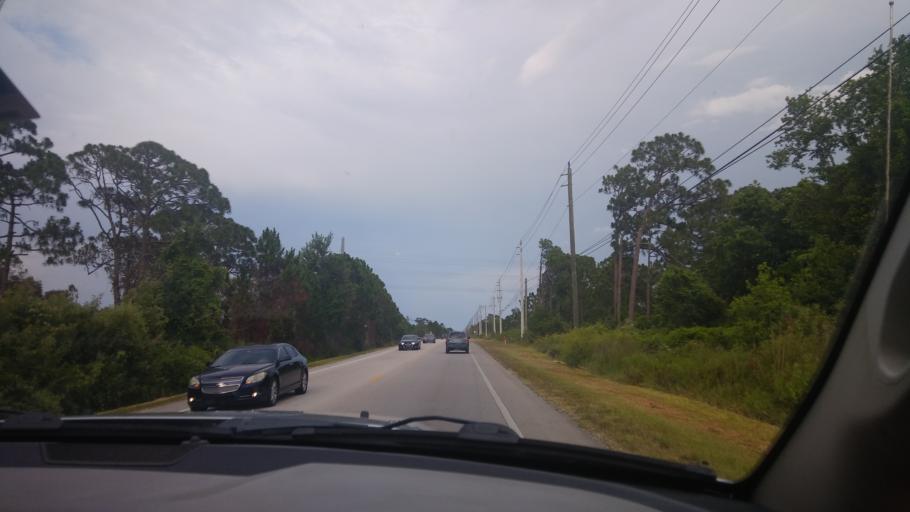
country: US
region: Florida
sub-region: Indian River County
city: Fellsmere
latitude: 27.7677
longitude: -80.5676
